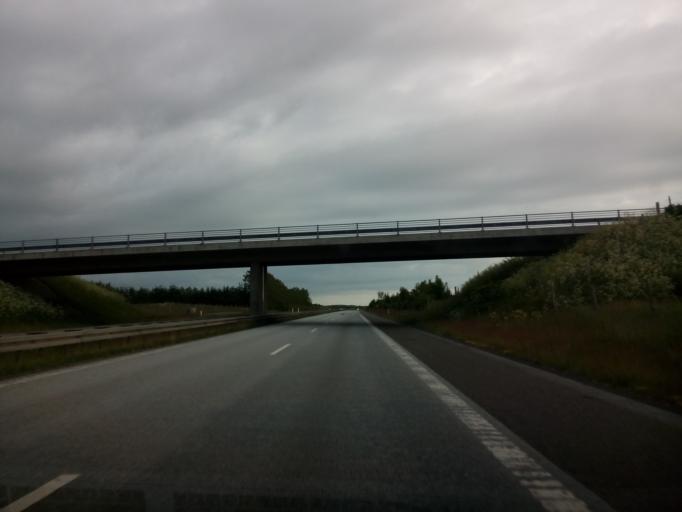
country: DK
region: North Denmark
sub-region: Hjorring Kommune
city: Vra
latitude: 57.3153
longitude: 10.0198
